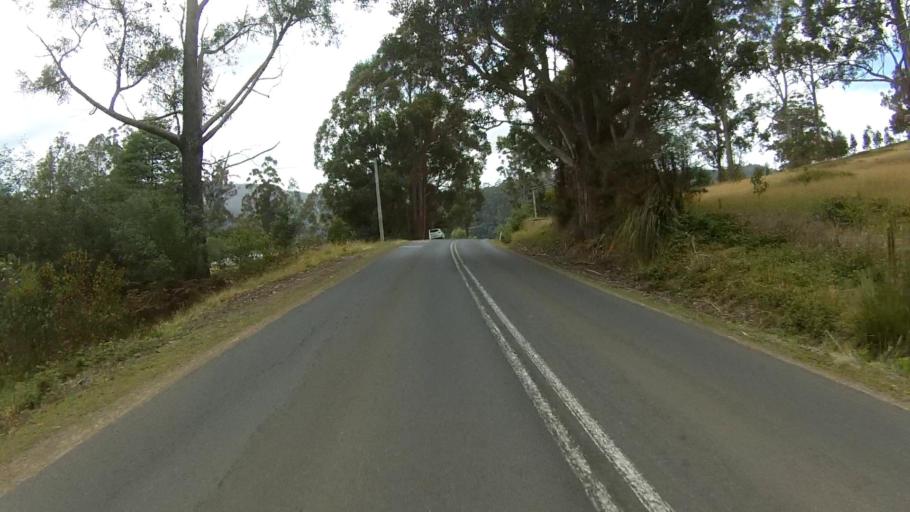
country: AU
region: Tasmania
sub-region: Huon Valley
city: Cygnet
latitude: -43.1375
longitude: 147.1523
